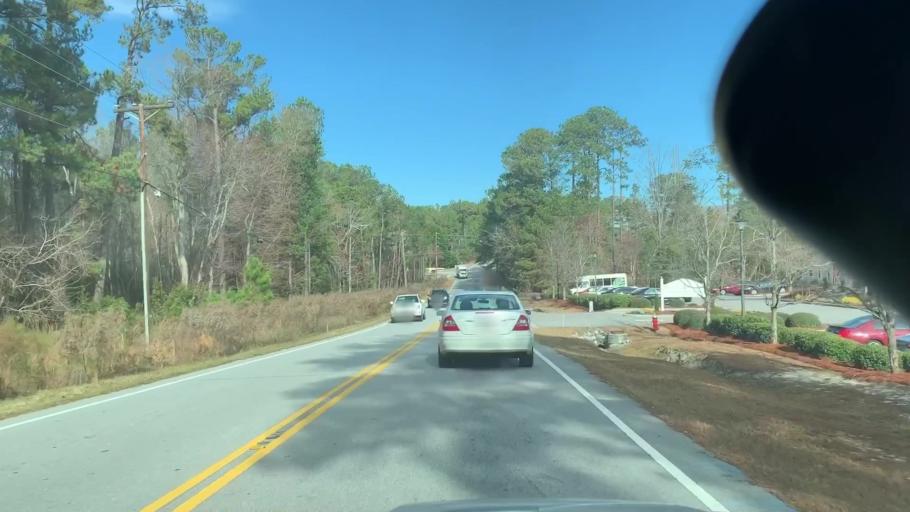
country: US
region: South Carolina
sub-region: Richland County
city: Woodfield
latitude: 34.0921
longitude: -80.8922
